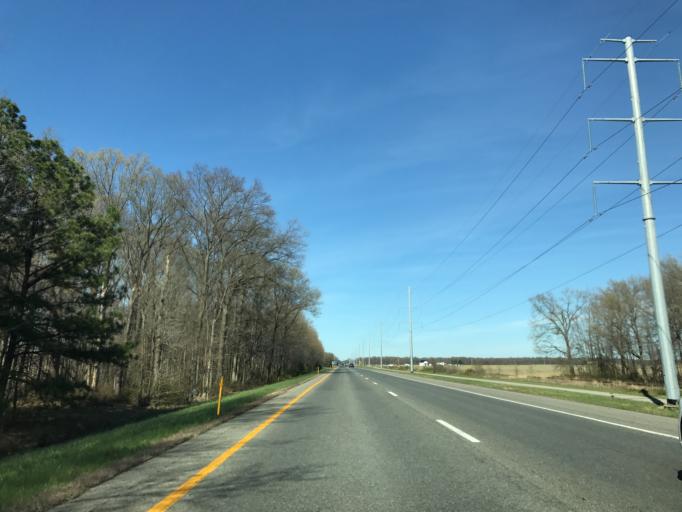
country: US
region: Maryland
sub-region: Queen Anne's County
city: Centreville
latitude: 39.0737
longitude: -75.9825
